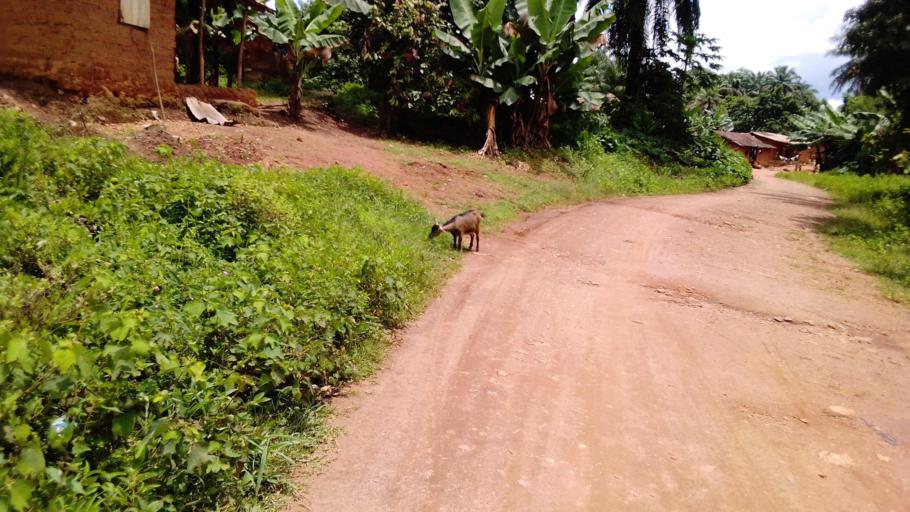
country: SL
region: Eastern Province
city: Koidu
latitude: 8.6737
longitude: -10.9378
